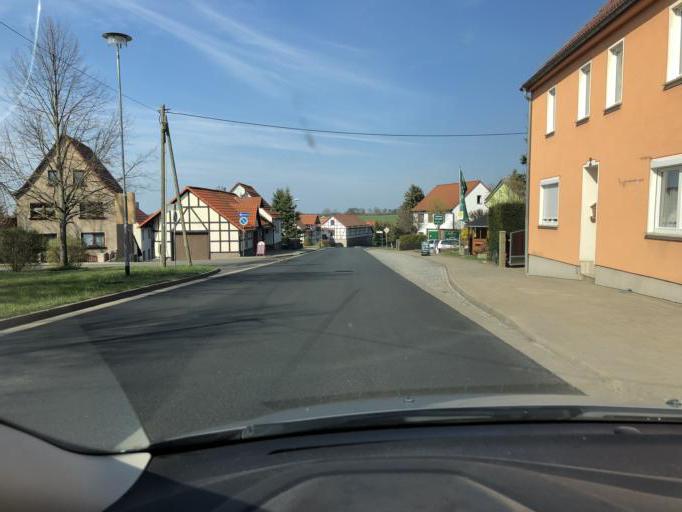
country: DE
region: Thuringia
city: Schwarza
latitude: 50.8119
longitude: 11.3361
